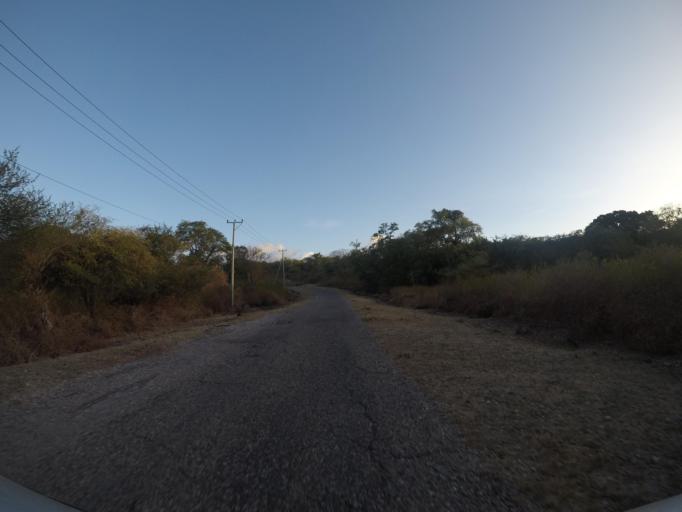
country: TL
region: Lautem
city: Lospalos
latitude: -8.3325
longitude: 127.0056
